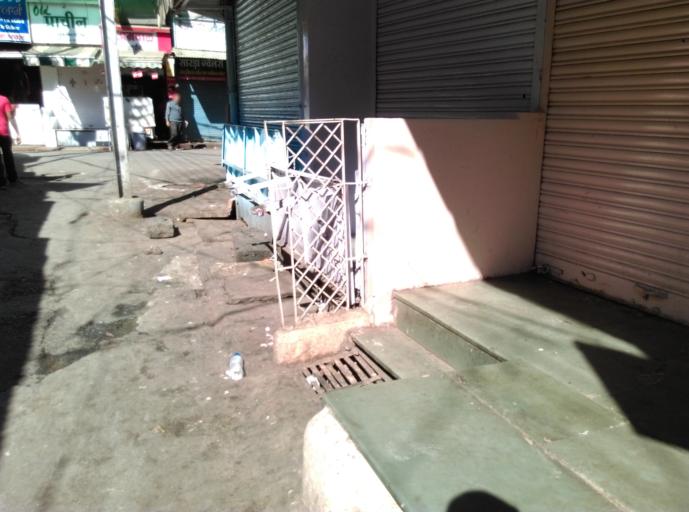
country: IN
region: Madhya Pradesh
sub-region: Indore
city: Indore
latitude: 22.7180
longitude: 75.8513
